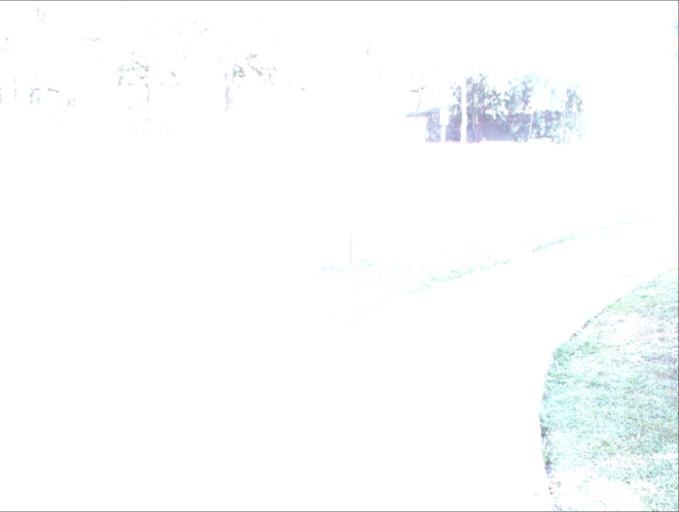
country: AU
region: Queensland
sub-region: Logan
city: Woodridge
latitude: -27.6317
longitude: 153.1029
